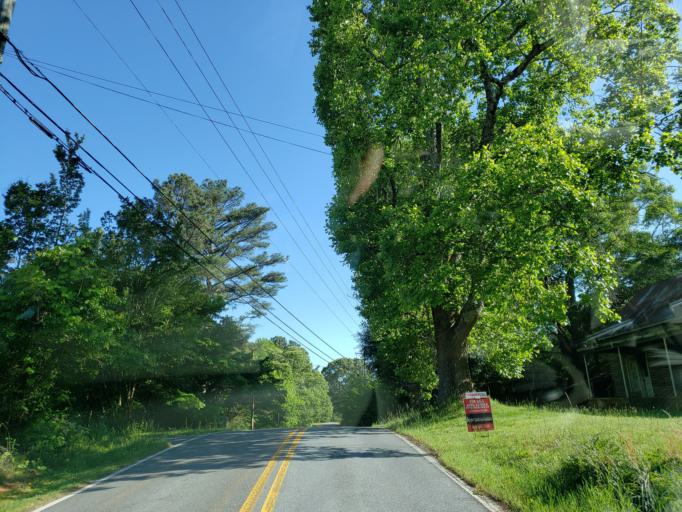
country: US
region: Georgia
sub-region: Paulding County
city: Hiram
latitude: 33.9097
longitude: -84.7936
